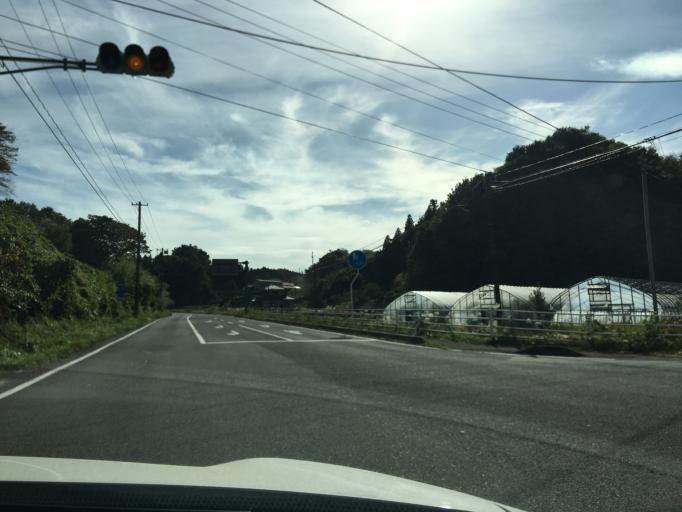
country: JP
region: Fukushima
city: Miharu
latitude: 37.4981
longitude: 140.4991
